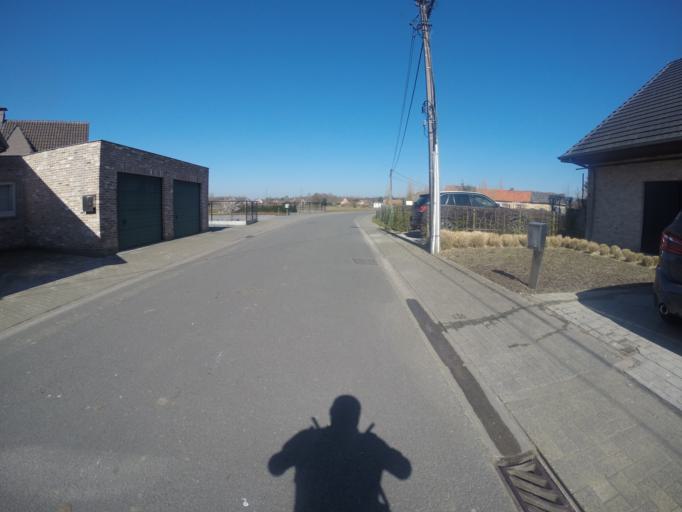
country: BE
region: Flanders
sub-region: Provincie West-Vlaanderen
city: Ruiselede
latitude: 51.0705
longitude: 3.3865
